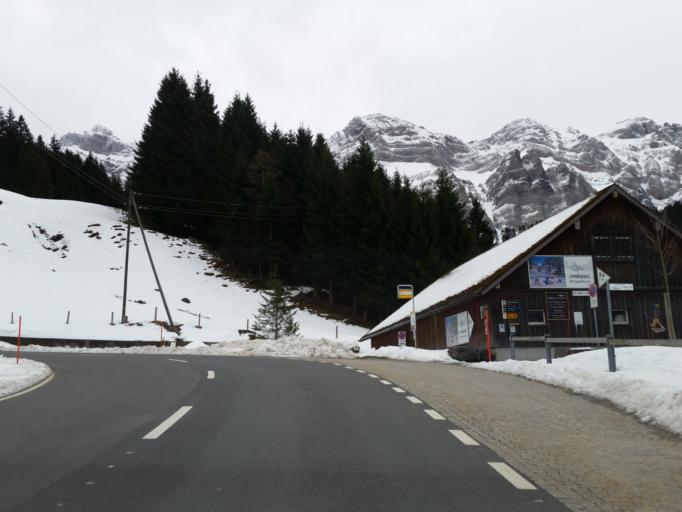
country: CH
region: Appenzell Ausserrhoden
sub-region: Bezirk Hinterland
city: Urnasch
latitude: 47.2631
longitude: 9.2985
